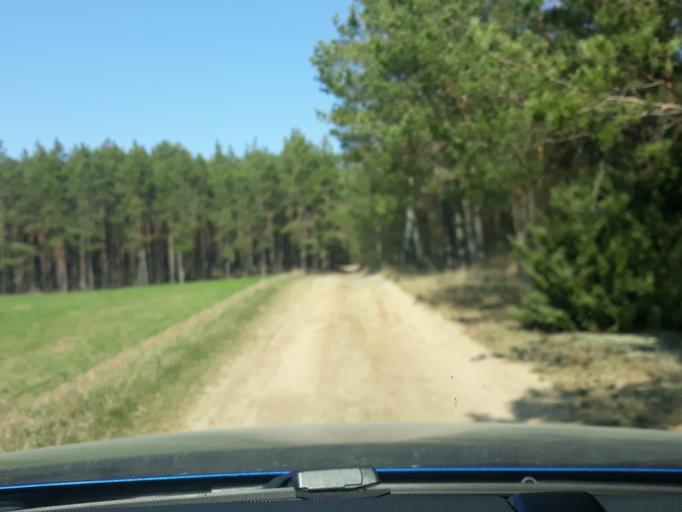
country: PL
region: Pomeranian Voivodeship
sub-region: Powiat bytowski
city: Lipnica
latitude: 53.8533
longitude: 17.4324
